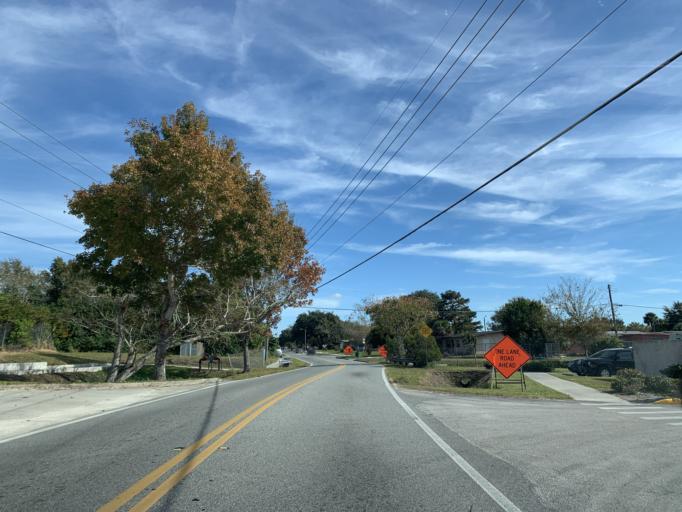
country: US
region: Florida
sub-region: Orange County
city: Tangelo Park
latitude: 28.4612
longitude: -81.4510
